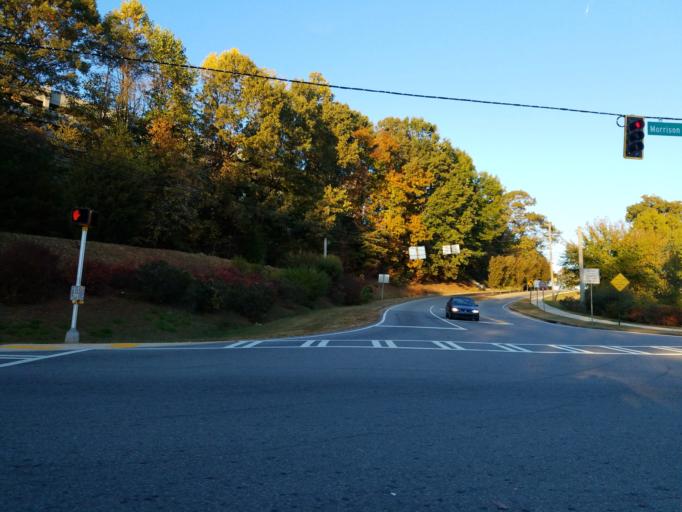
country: US
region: Georgia
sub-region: Lumpkin County
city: Dahlonega
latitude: 34.5268
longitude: -83.9909
